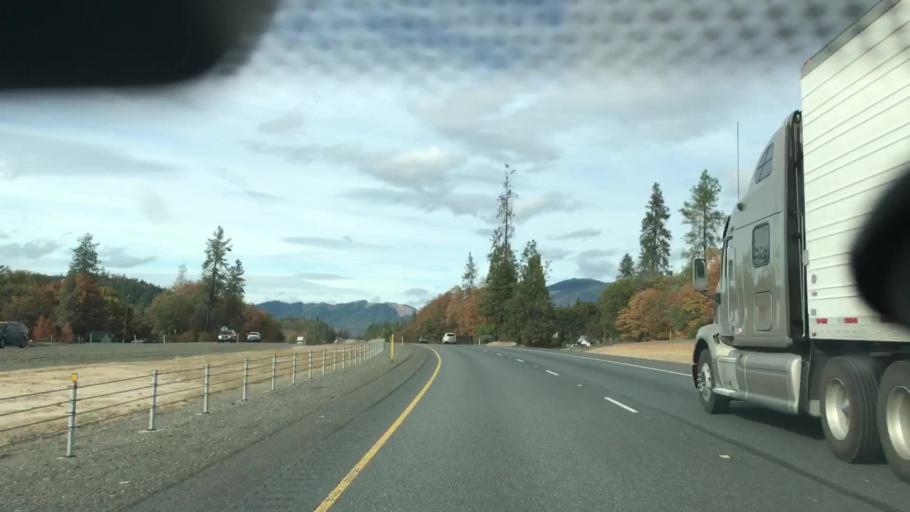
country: US
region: Oregon
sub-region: Josephine County
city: Merlin
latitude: 42.5144
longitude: -123.3632
